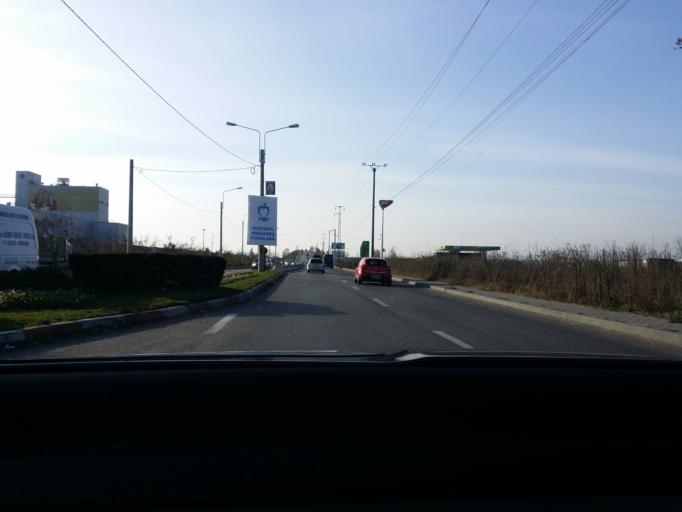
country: RO
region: Prahova
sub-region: Comuna Targsoru Vechi
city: Strejnicu
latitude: 44.9396
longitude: 25.9746
